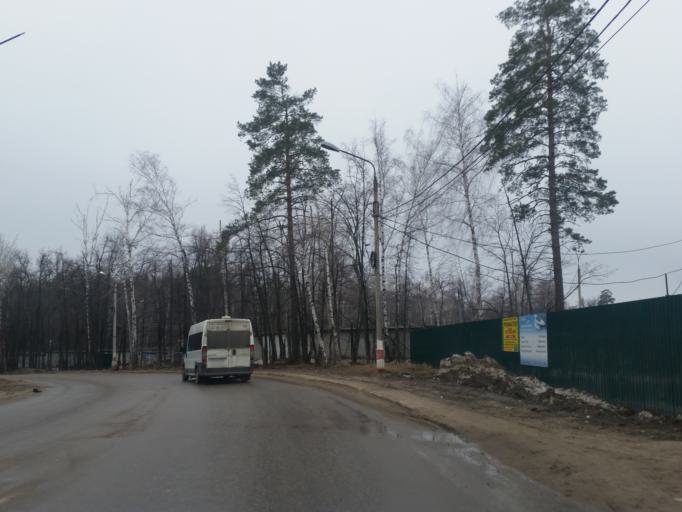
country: RU
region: Ulyanovsk
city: Dimitrovgrad
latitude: 54.2211
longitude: 49.5463
